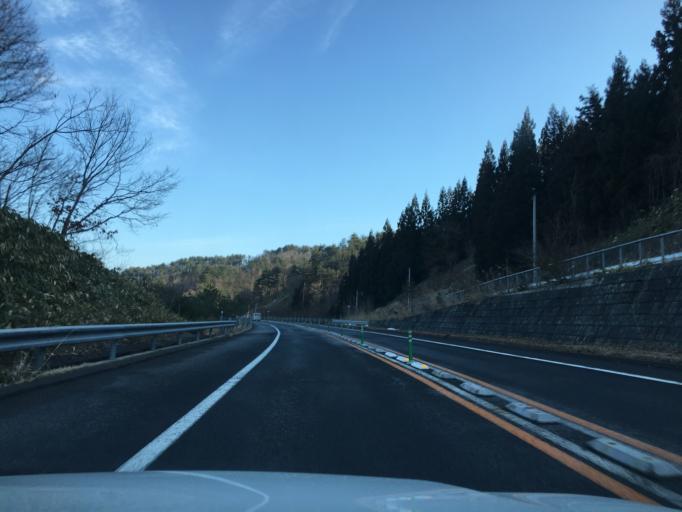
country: JP
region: Yamagata
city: Sagae
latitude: 38.4067
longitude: 140.1917
